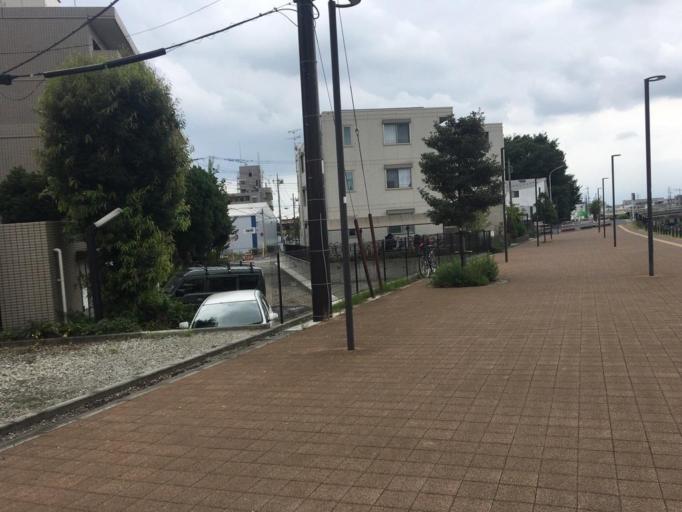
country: JP
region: Saitama
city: Shimotoda
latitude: 35.8190
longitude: 139.6591
